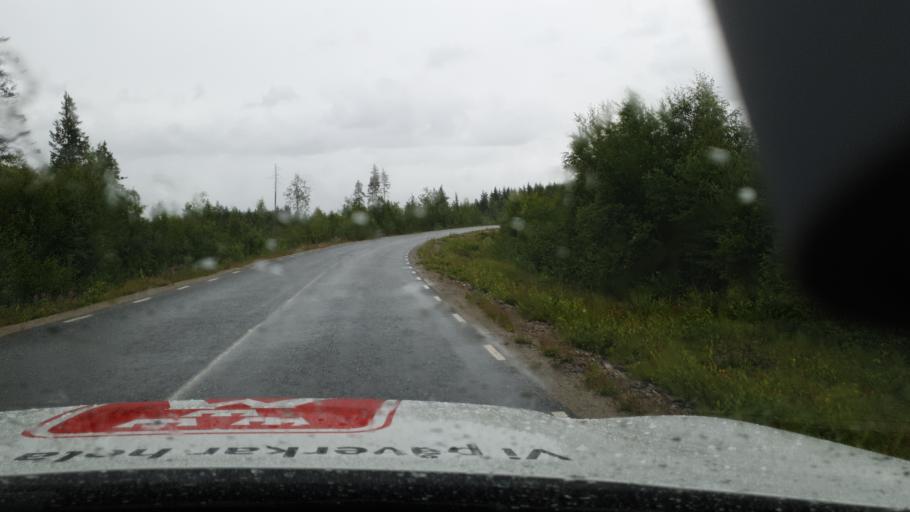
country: SE
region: Vaesterbotten
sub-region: Vindelns Kommun
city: Vindeln
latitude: 64.4863
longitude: 19.7753
